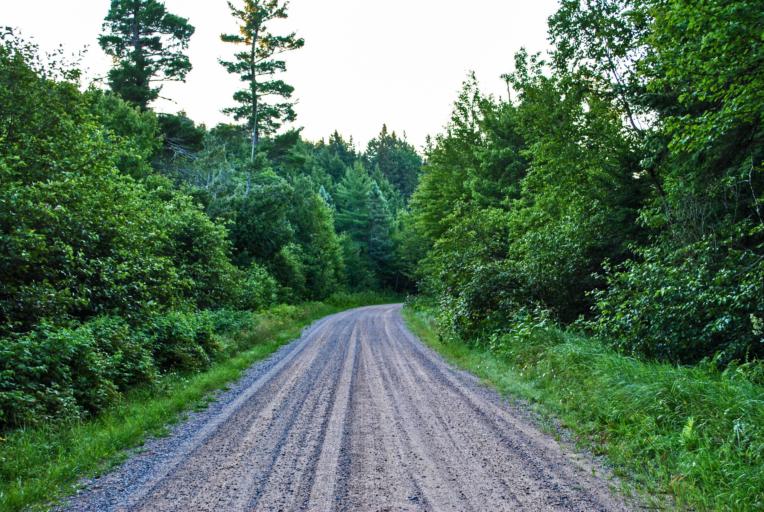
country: US
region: Wisconsin
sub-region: Forest County
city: Crandon
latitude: 45.7754
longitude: -89.0187
